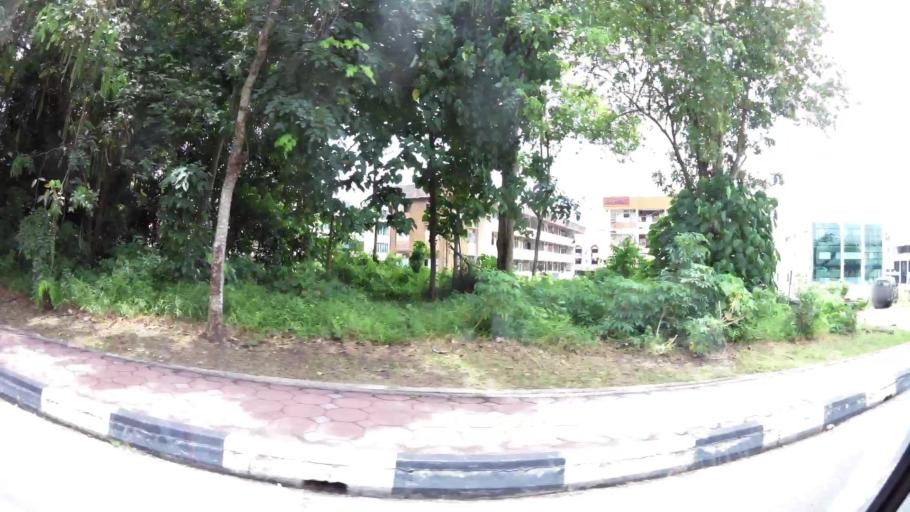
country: BN
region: Brunei and Muara
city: Bandar Seri Begawan
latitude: 4.9102
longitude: 114.9179
